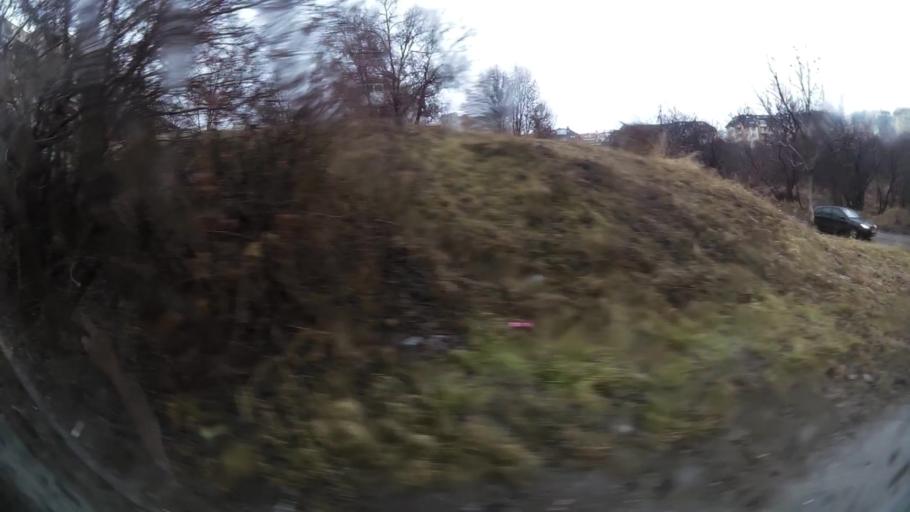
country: BG
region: Sofia-Capital
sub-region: Stolichna Obshtina
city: Sofia
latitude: 42.6581
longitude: 23.3727
